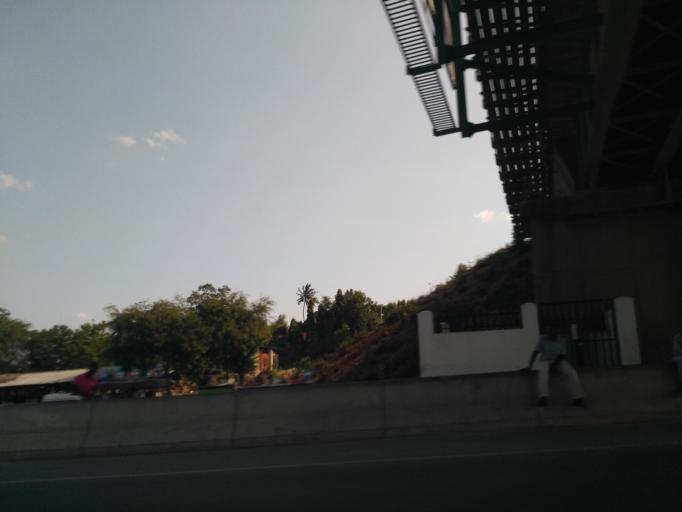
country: TZ
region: Dar es Salaam
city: Dar es Salaam
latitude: -6.8591
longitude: 39.2916
